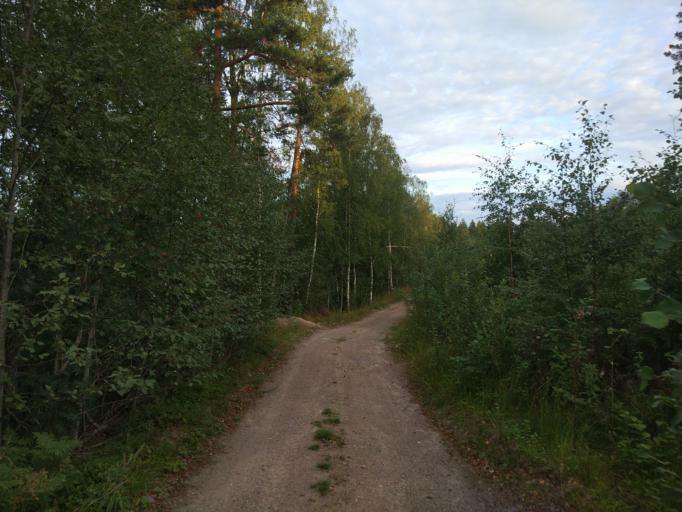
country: RU
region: Leningrad
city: Kuznechnoye
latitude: 61.1153
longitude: 29.6063
